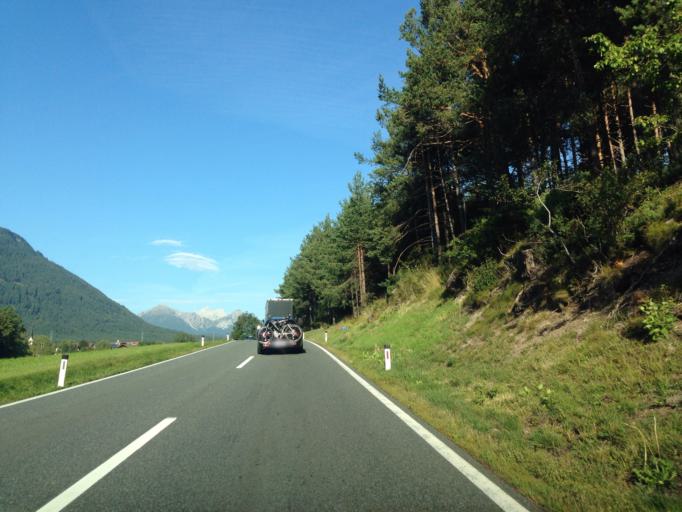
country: AT
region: Tyrol
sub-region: Politischer Bezirk Imst
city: Obsteig
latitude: 47.2987
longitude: 10.9384
